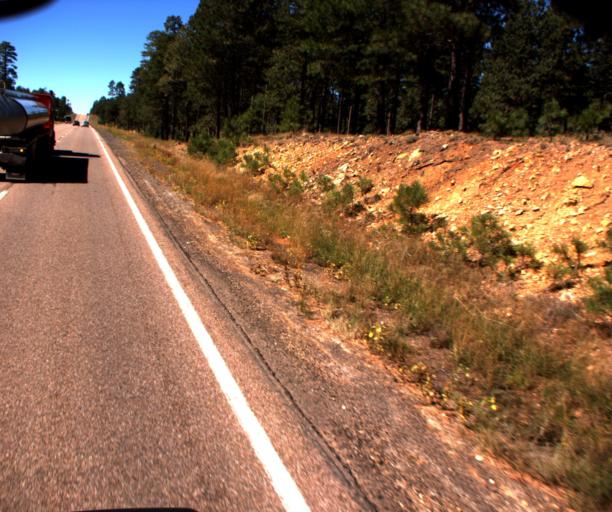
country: US
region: Arizona
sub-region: Navajo County
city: Heber-Overgaard
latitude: 34.3278
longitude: -110.8172
